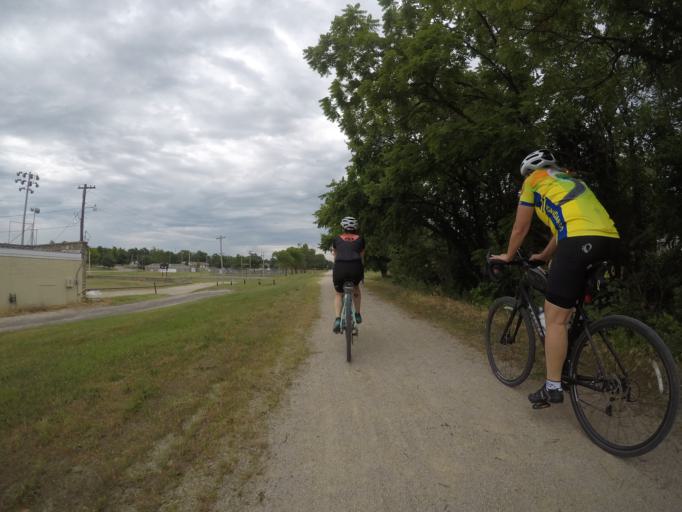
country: US
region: Kansas
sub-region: Anderson County
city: Garnett
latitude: 38.2900
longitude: -95.2417
